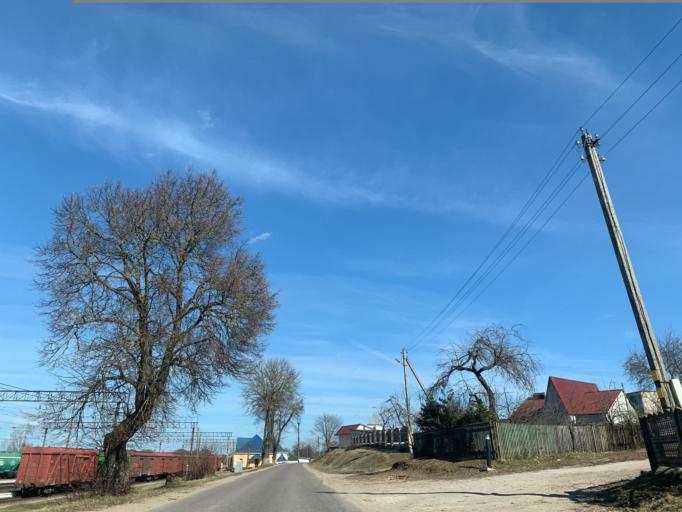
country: BY
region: Minsk
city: Haradzyeya
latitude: 53.3126
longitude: 26.5357
